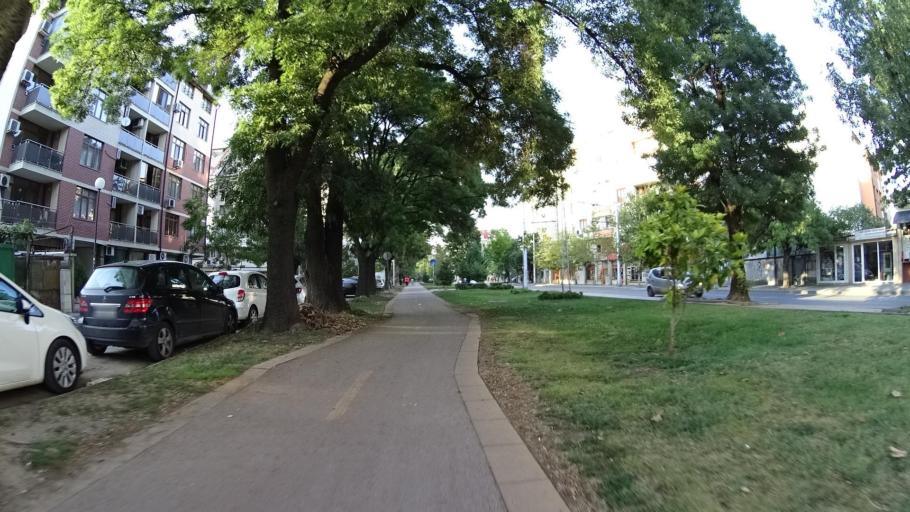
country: BG
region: Plovdiv
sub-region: Obshtina Plovdiv
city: Plovdiv
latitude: 42.1273
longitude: 24.7423
